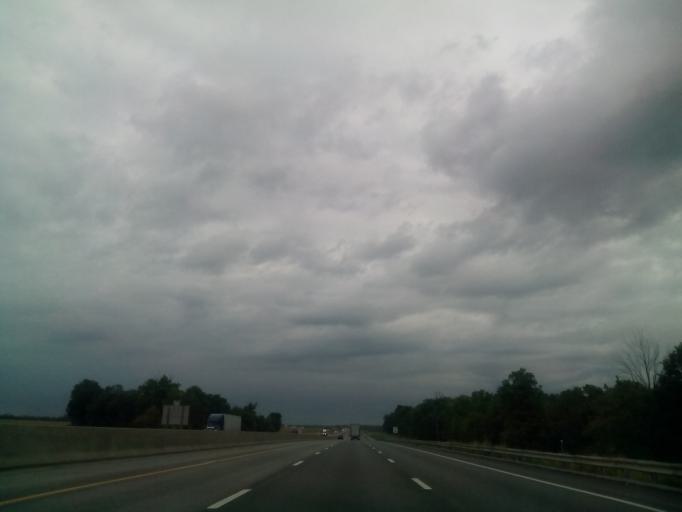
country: US
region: Ohio
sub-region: Ottawa County
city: Genoa
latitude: 41.4852
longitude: -83.3577
